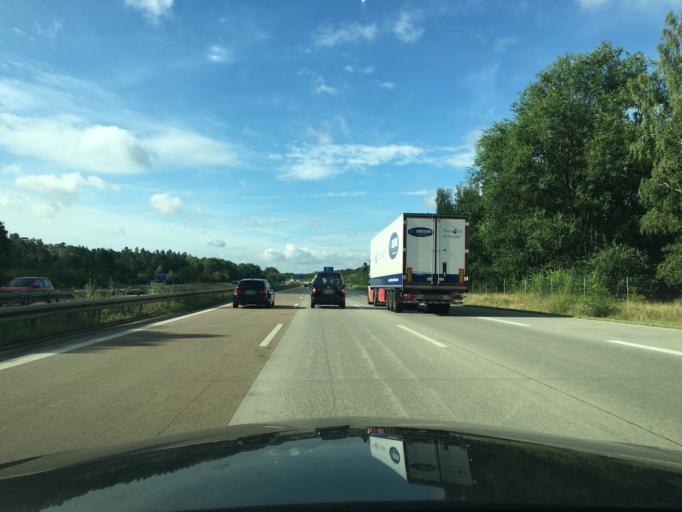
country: DE
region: Berlin
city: Wannsee
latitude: 52.3872
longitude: 13.1543
